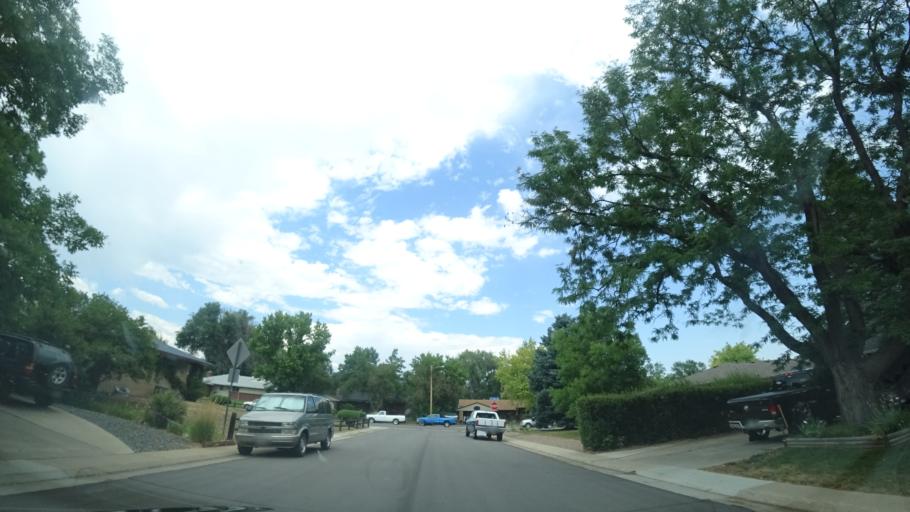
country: US
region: Colorado
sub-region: Jefferson County
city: Lakewood
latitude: 39.7193
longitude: -105.0991
